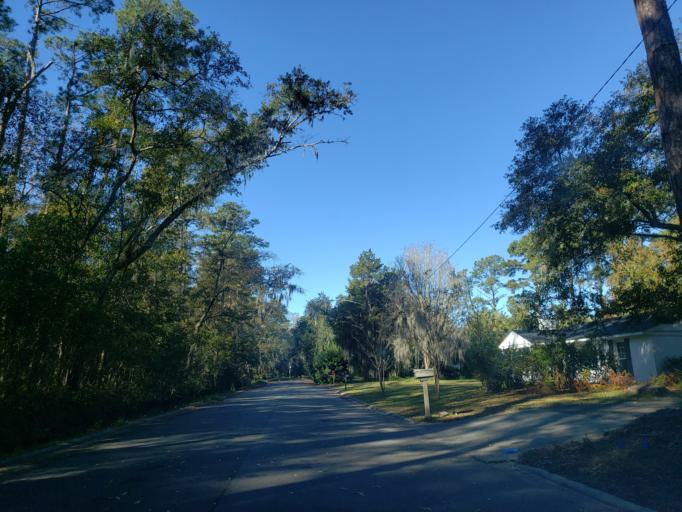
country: US
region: Georgia
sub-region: Chatham County
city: Isle of Hope
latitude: 31.9806
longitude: -81.0679
